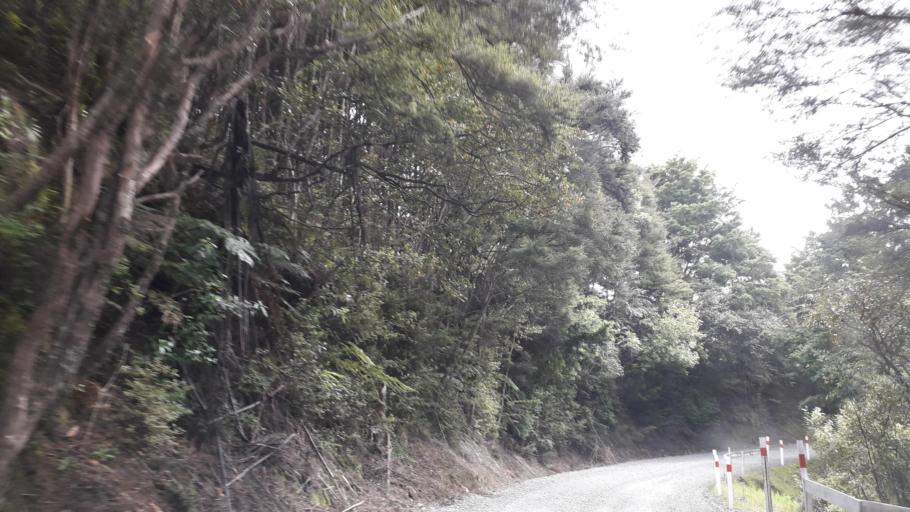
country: NZ
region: Northland
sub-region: Far North District
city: Waimate North
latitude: -35.1334
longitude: 173.7166
